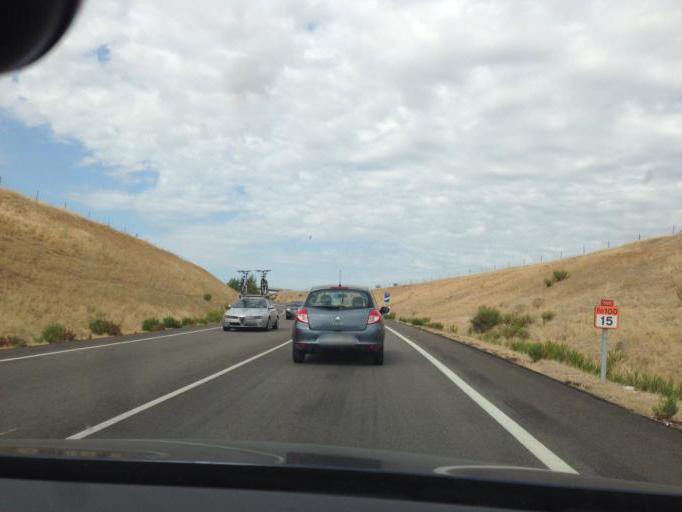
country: ES
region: Madrid
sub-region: Provincia de Madrid
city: Cobena
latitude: 40.5559
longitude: -3.4882
